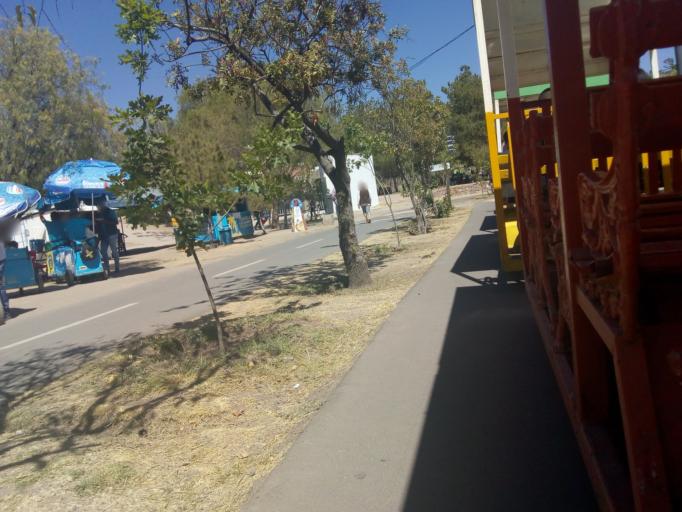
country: MX
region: Guanajuato
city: Leon
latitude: 21.1882
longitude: -101.6806
